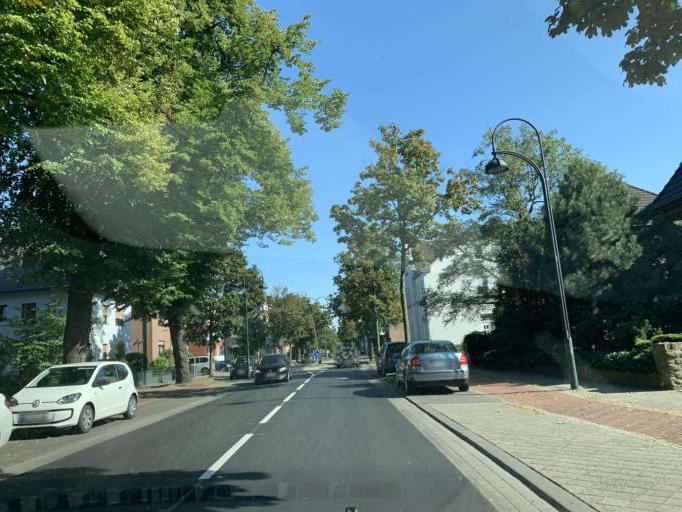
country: DE
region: North Rhine-Westphalia
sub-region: Regierungsbezirk Arnsberg
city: Hamm
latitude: 51.6877
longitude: 7.8437
